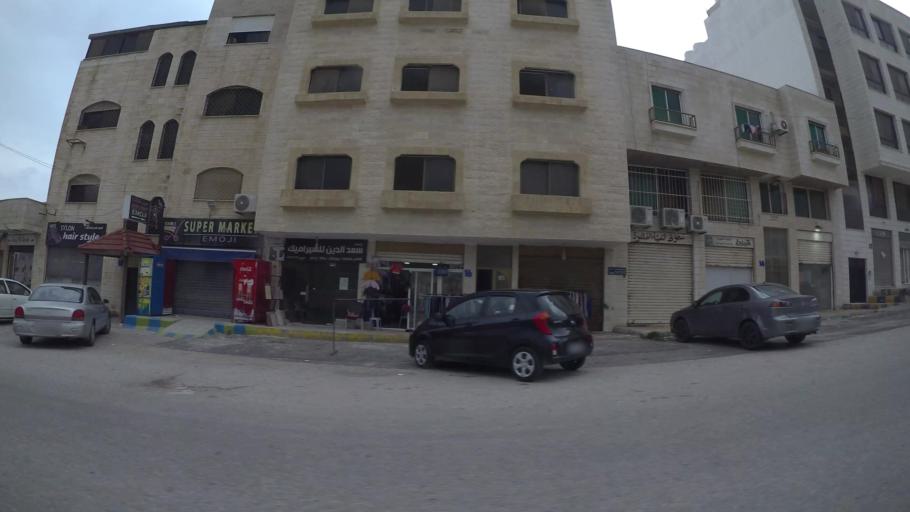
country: JO
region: Amman
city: Umm as Summaq
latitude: 31.8851
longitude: 35.8549
